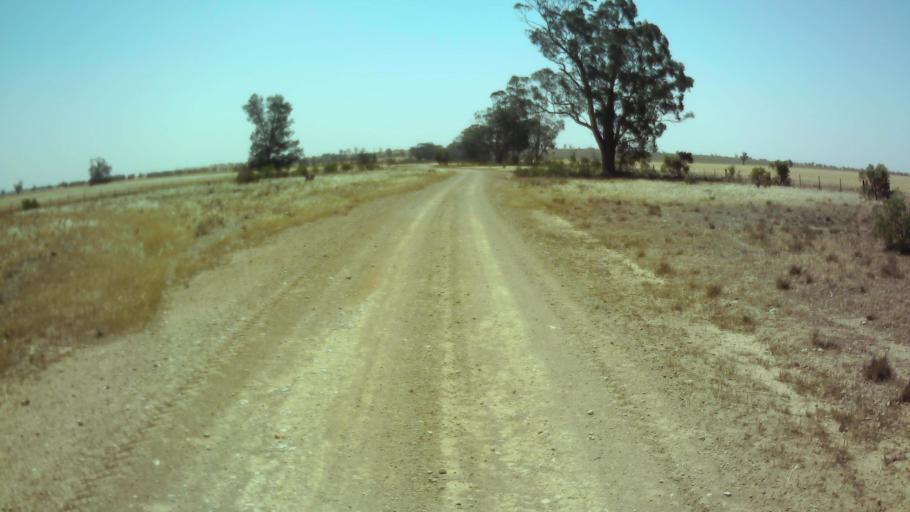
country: AU
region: New South Wales
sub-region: Weddin
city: Grenfell
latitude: -33.9152
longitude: 147.7729
